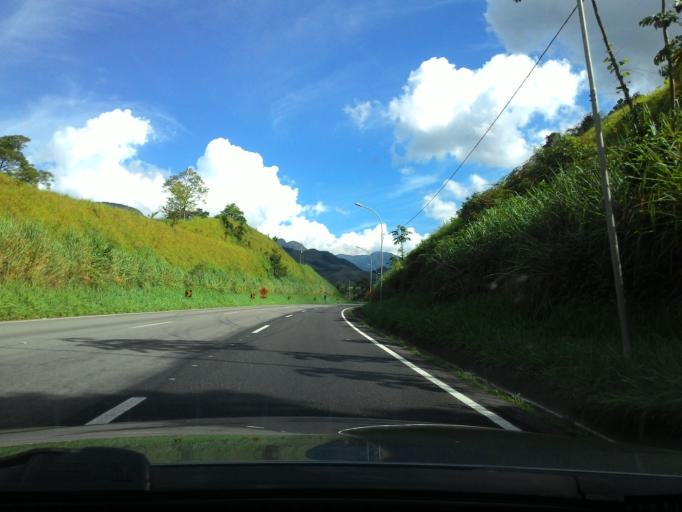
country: BR
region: Sao Paulo
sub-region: Cajati
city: Cajati
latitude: -24.8130
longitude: -48.2130
